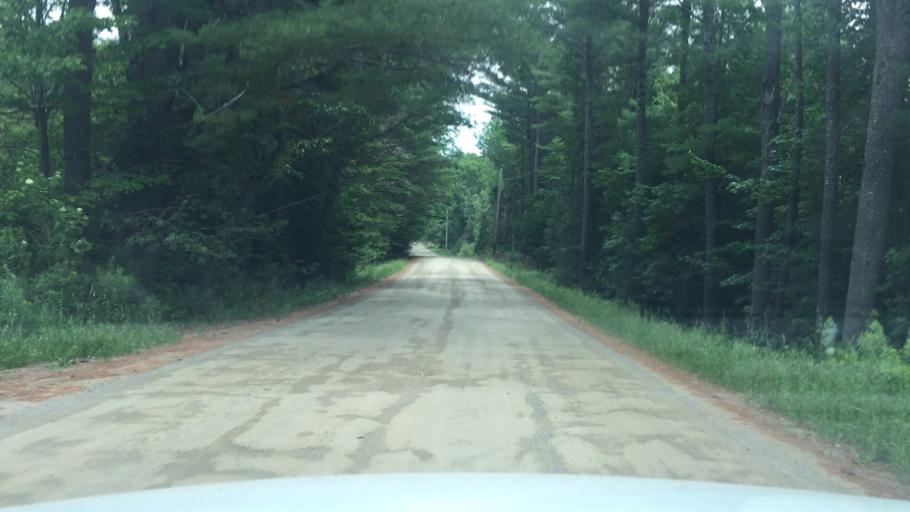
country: US
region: Maine
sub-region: Kennebec County
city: Albion
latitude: 44.4563
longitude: -69.3252
